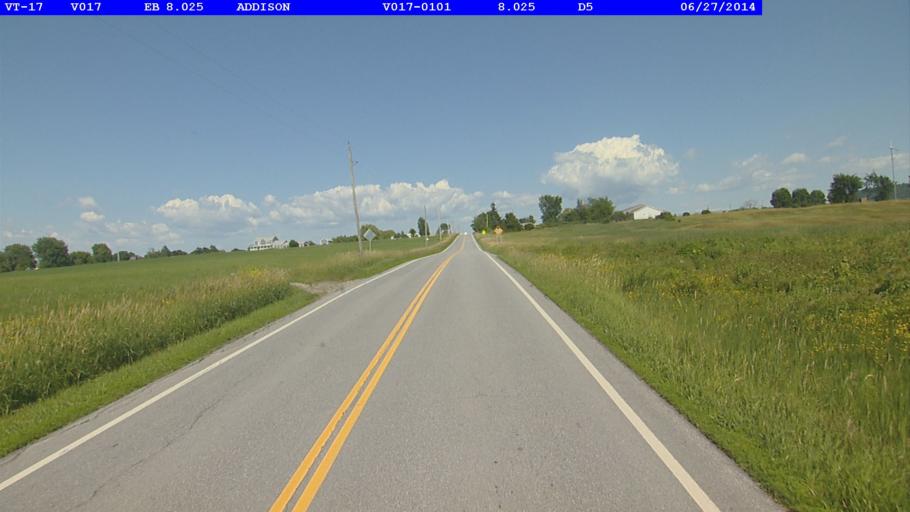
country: US
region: Vermont
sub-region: Addison County
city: Vergennes
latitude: 44.0884
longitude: -73.3094
